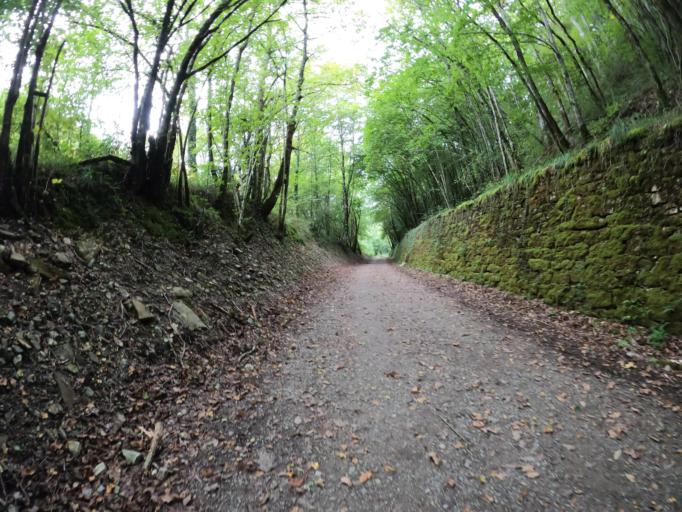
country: ES
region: Navarre
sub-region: Provincia de Navarra
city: Lekunberri
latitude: 42.9834
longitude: -1.8693
